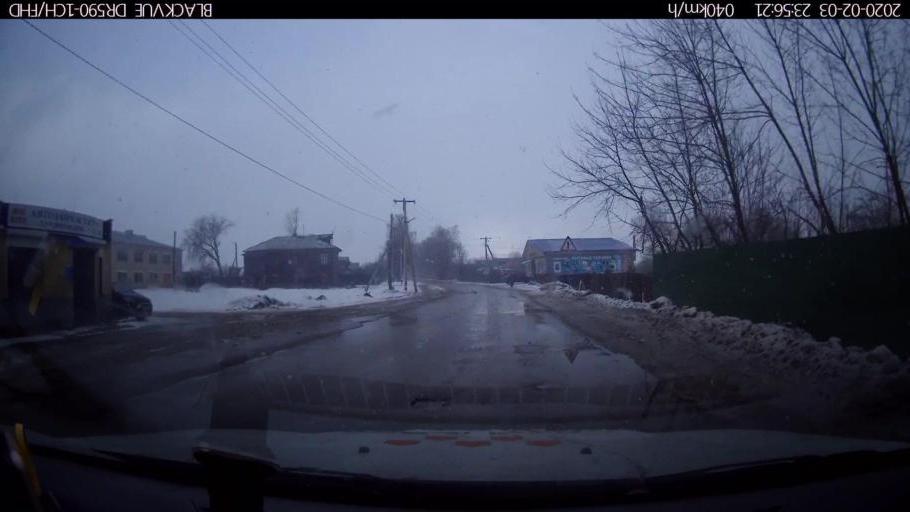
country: RU
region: Nizjnij Novgorod
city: Dal'neye Konstantinovo
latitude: 55.8089
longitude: 44.0875
